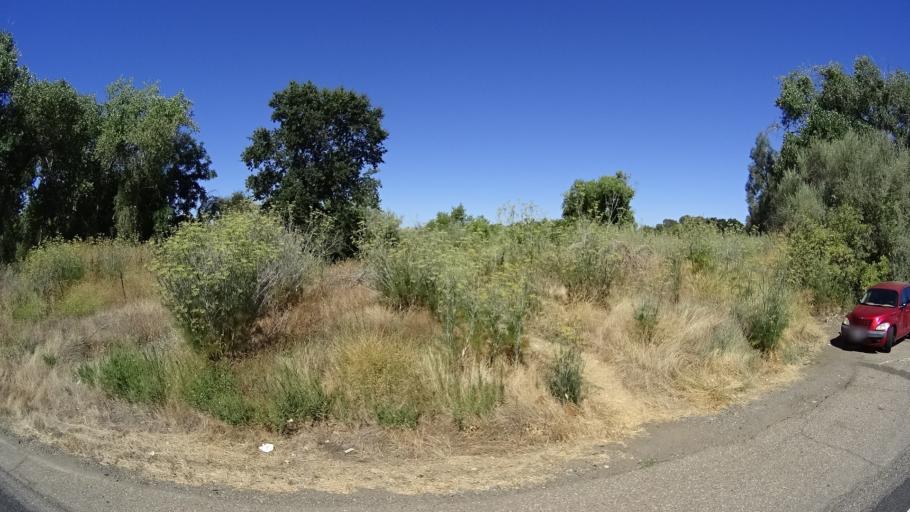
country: US
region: California
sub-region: Calaveras County
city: Rancho Calaveras
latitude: 38.0938
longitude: -120.8721
